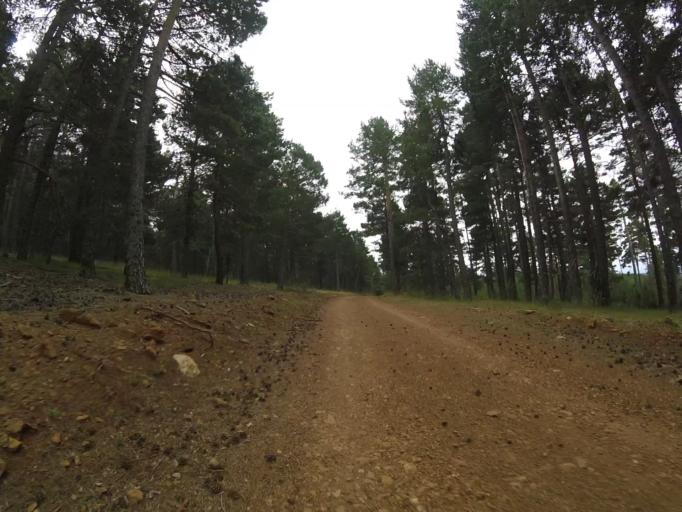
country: ES
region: Aragon
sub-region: Provincia de Teruel
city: Valdelinares
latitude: 40.3674
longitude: -0.6187
